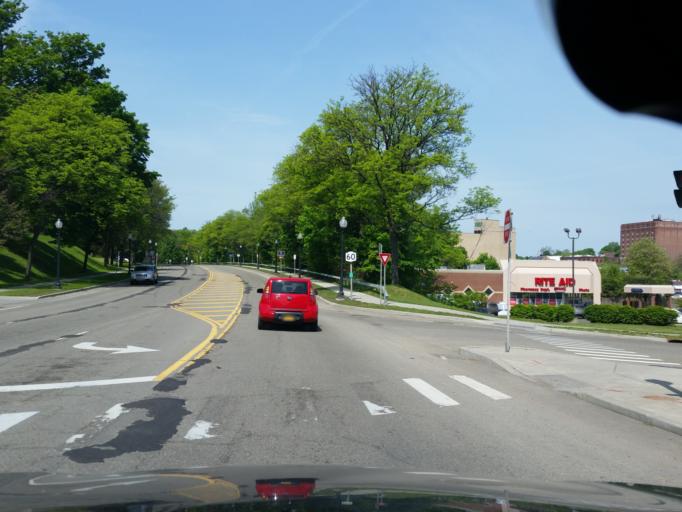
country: US
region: New York
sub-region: Chautauqua County
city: Jamestown
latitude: 42.0920
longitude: -79.2374
